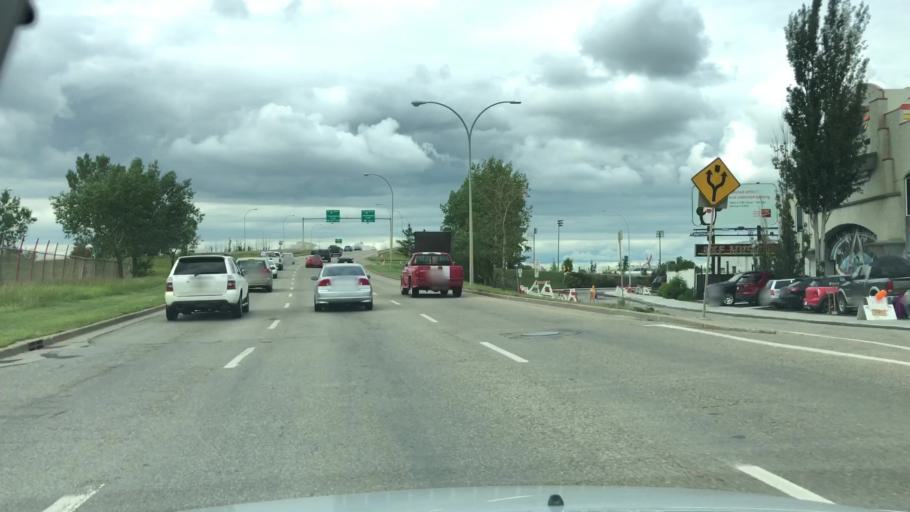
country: CA
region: Alberta
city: Edmonton
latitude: 53.5726
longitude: -113.4522
